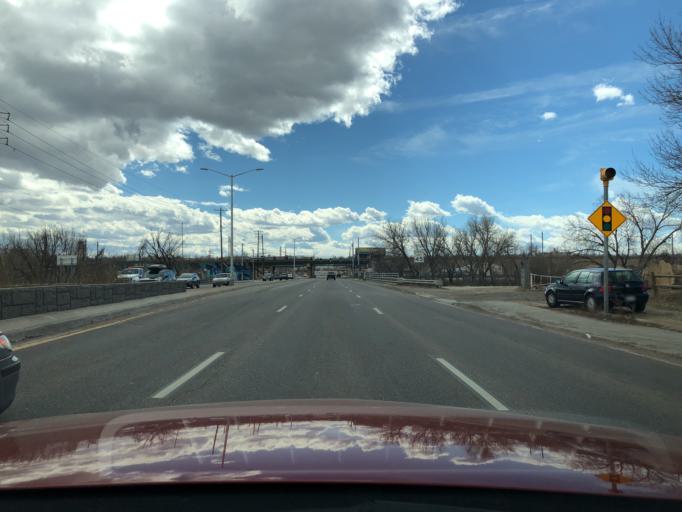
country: US
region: Colorado
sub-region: Adams County
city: Berkley
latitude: 39.8062
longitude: -105.0254
